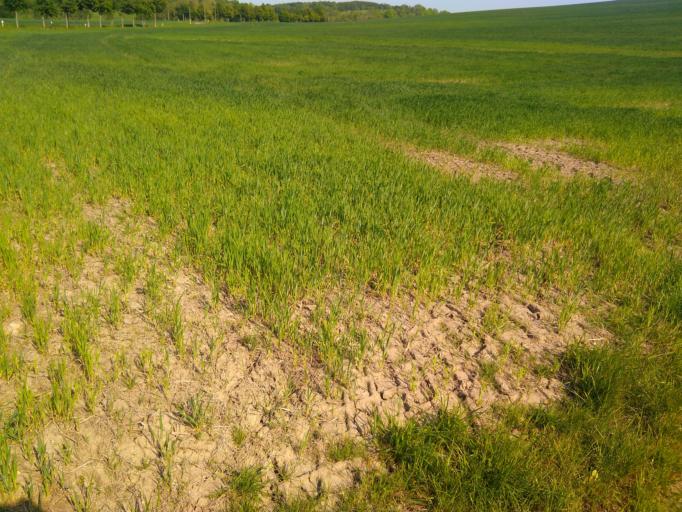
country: DE
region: Thuringia
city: Petersberg
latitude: 50.9950
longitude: 11.8493
